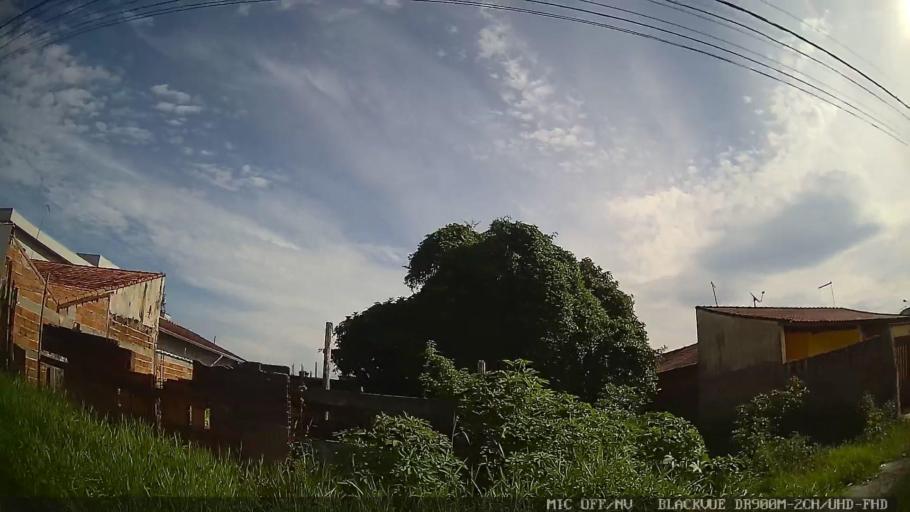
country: BR
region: Sao Paulo
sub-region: Itanhaem
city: Itanhaem
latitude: -24.1540
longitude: -46.7764
